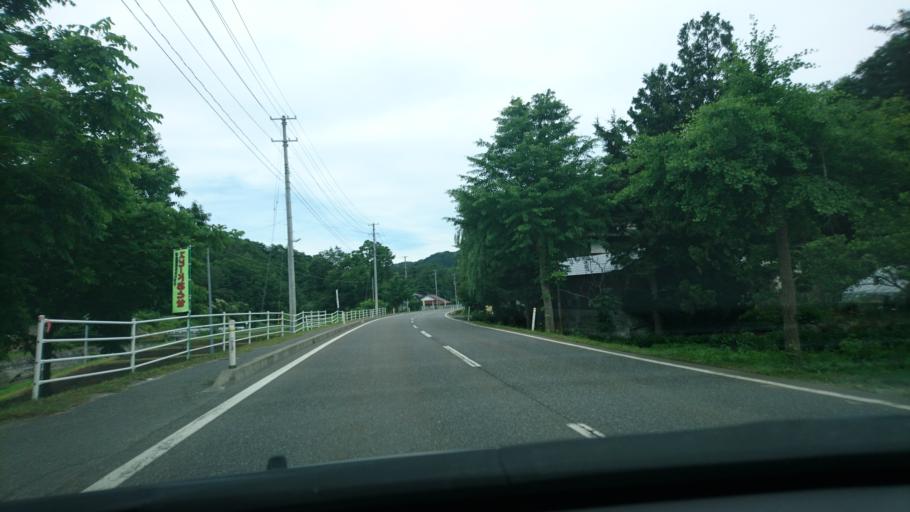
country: JP
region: Iwate
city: Miyako
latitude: 39.9619
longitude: 141.8496
